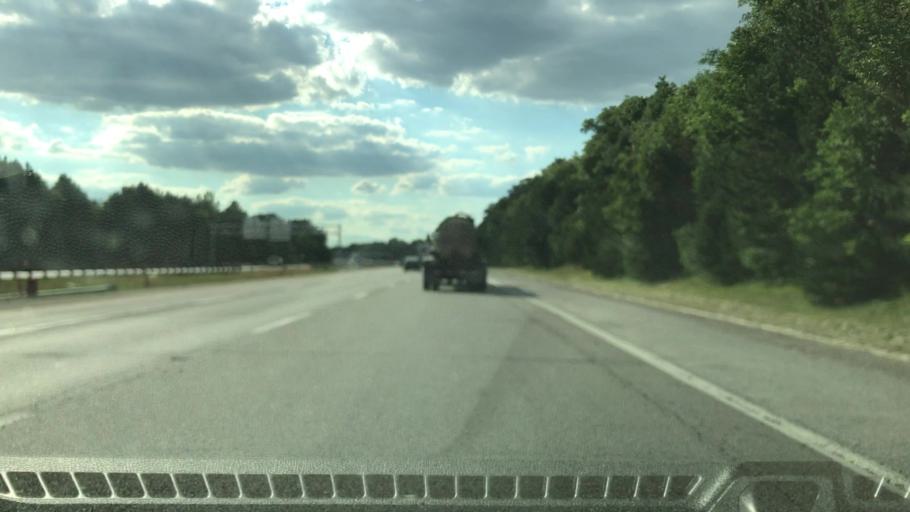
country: US
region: Ohio
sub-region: Franklin County
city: Grove City
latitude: 39.8961
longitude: -83.0455
